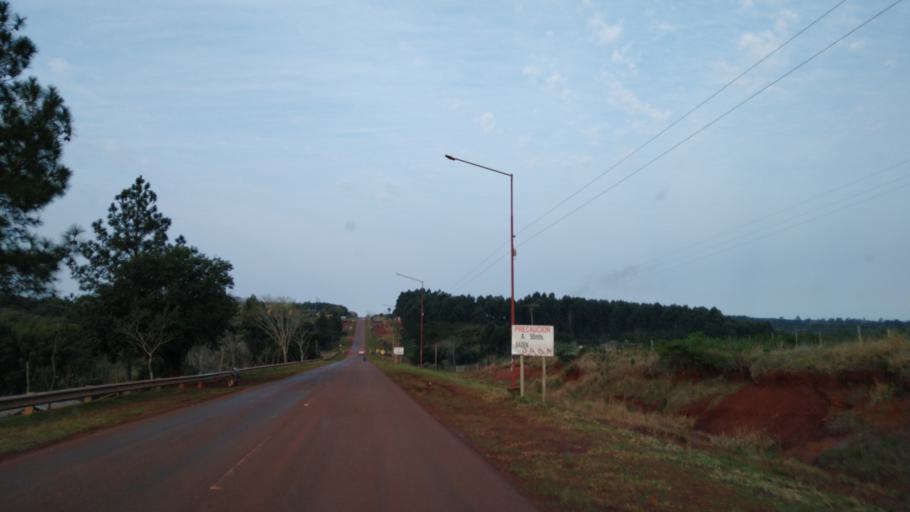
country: AR
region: Corrientes
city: San Carlos
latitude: -27.7519
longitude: -55.8940
